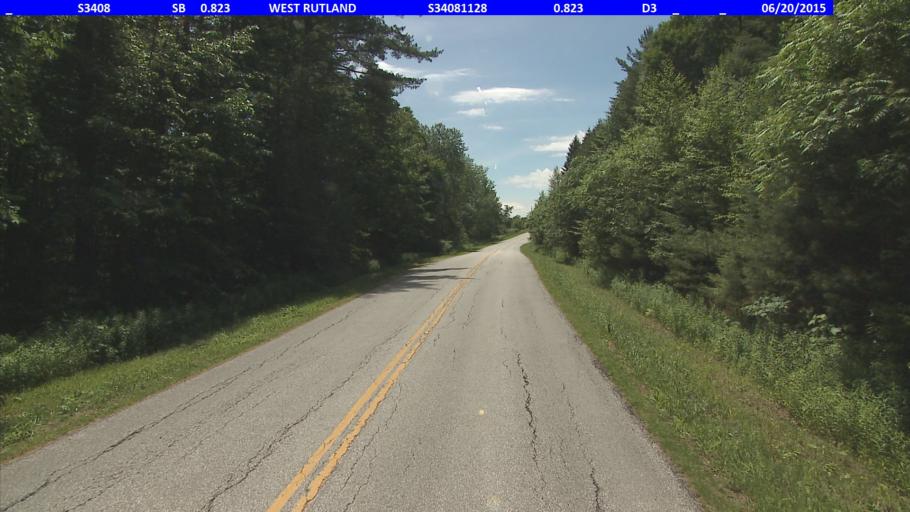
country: US
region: Vermont
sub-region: Rutland County
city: West Rutland
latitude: 43.6218
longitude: -73.0659
